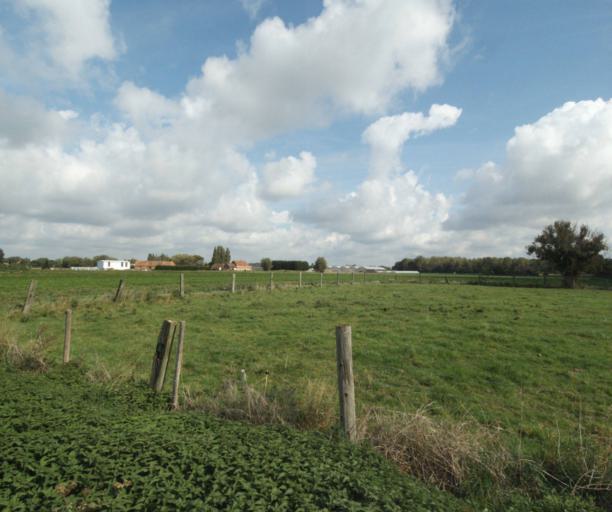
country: FR
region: Nord-Pas-de-Calais
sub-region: Departement du Nord
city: Perenchies
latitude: 50.6781
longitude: 2.9710
